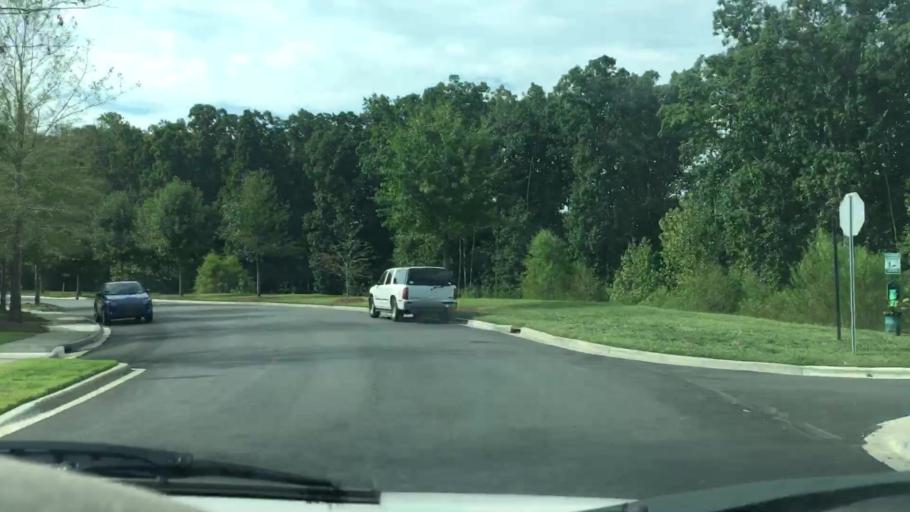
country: US
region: North Carolina
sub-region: Mecklenburg County
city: Huntersville
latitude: 35.4472
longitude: -80.7764
